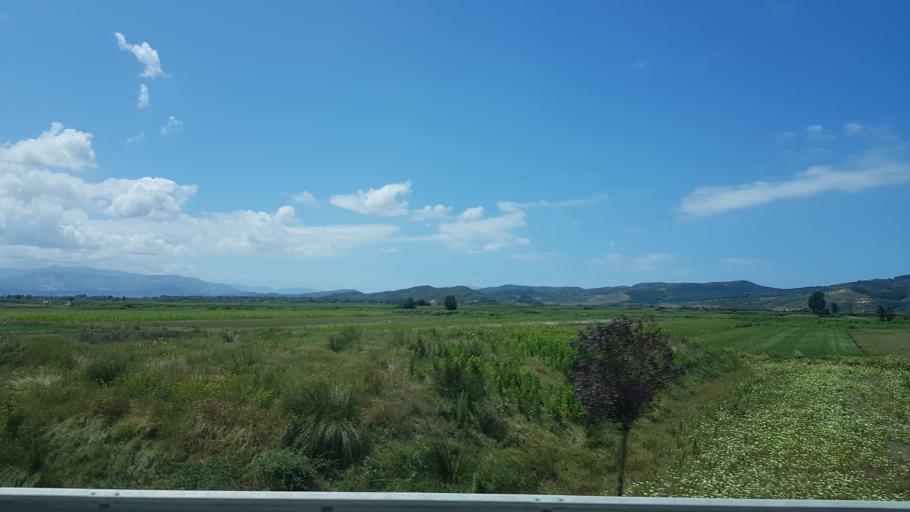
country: AL
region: Fier
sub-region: Rrethi i Fierit
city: Cakran
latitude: 40.5975
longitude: 19.5674
